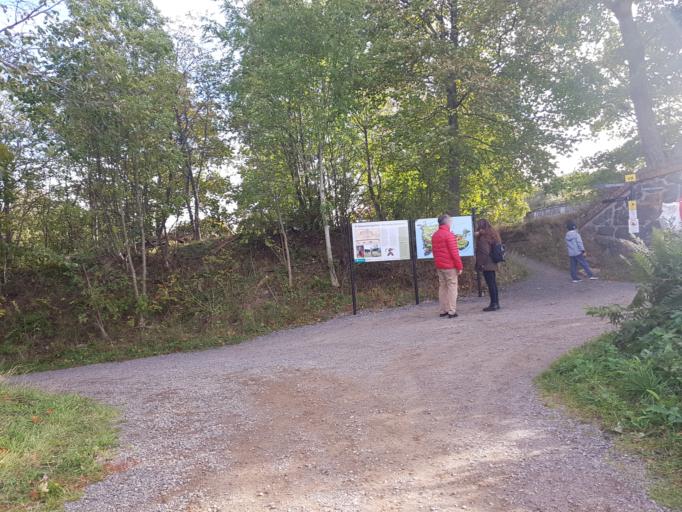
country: FI
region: Uusimaa
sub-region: Helsinki
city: Helsinki
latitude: 60.1353
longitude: 24.9995
